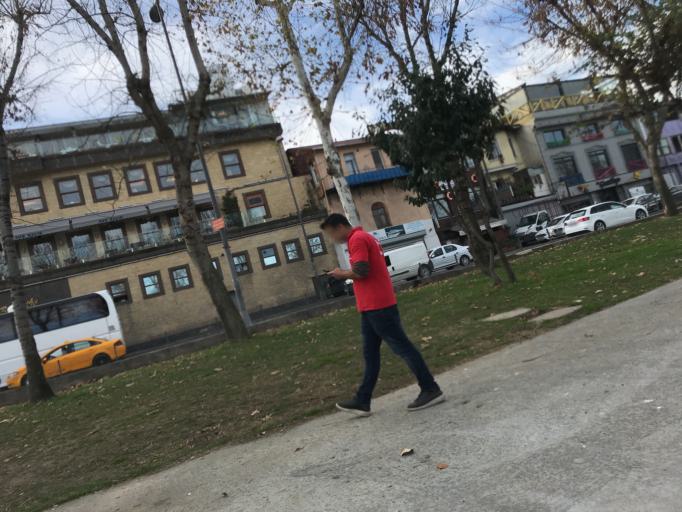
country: TR
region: Istanbul
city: Istanbul
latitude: 41.0258
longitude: 28.9594
